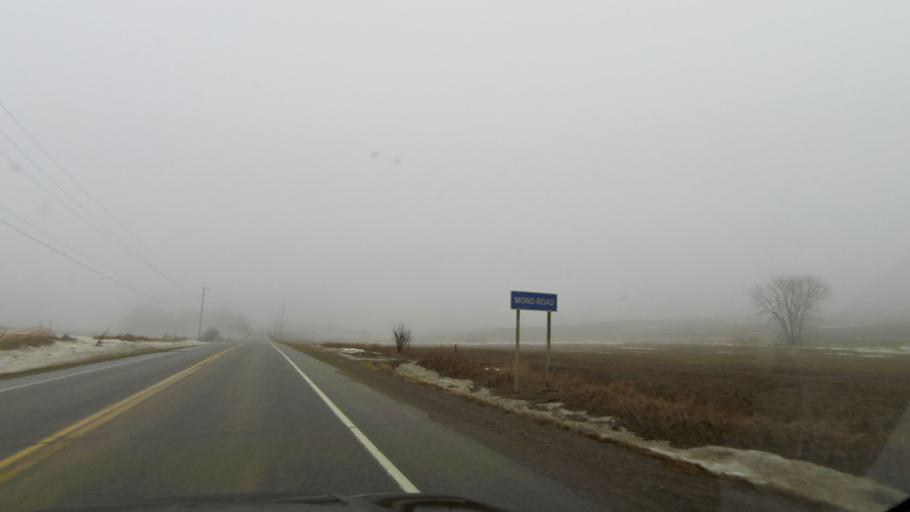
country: CA
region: Ontario
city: Brampton
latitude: 43.8506
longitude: -79.8599
